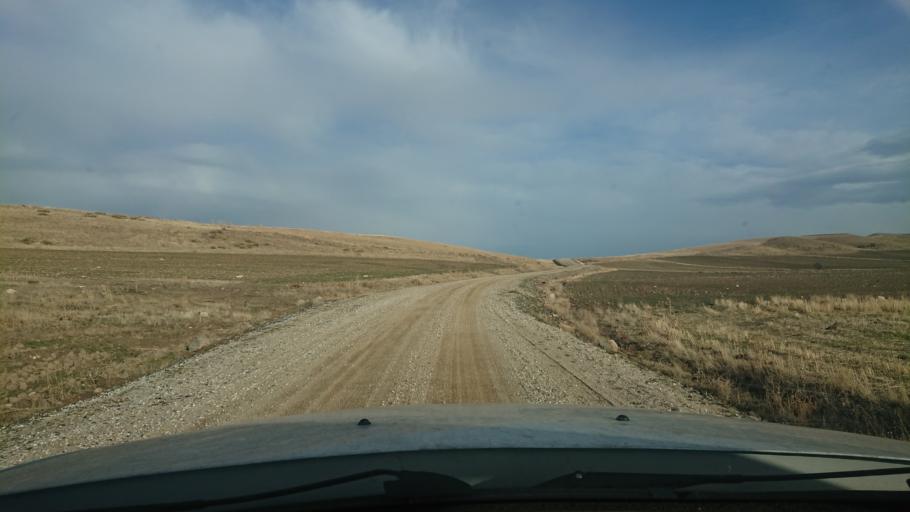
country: TR
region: Aksaray
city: Acipinar
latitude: 38.6856
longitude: 33.8696
